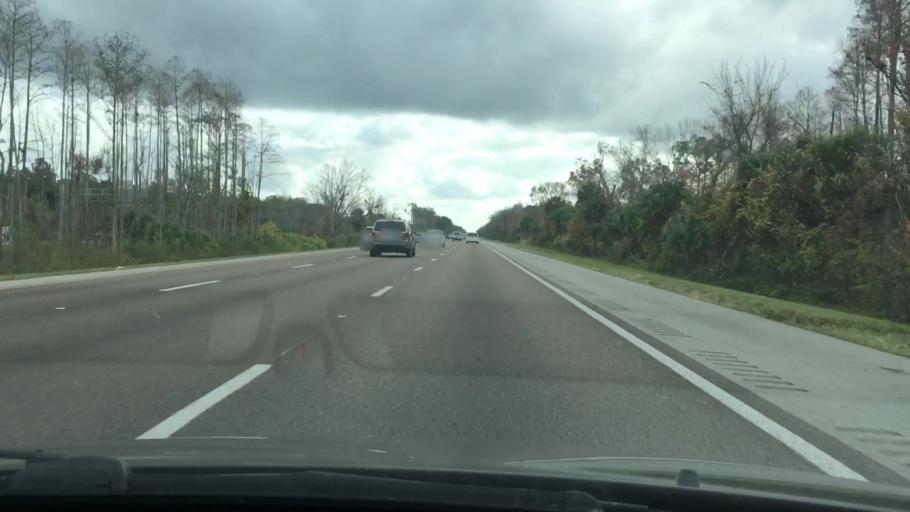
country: US
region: Florida
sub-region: Volusia County
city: Glencoe
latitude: 28.9976
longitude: -80.9783
